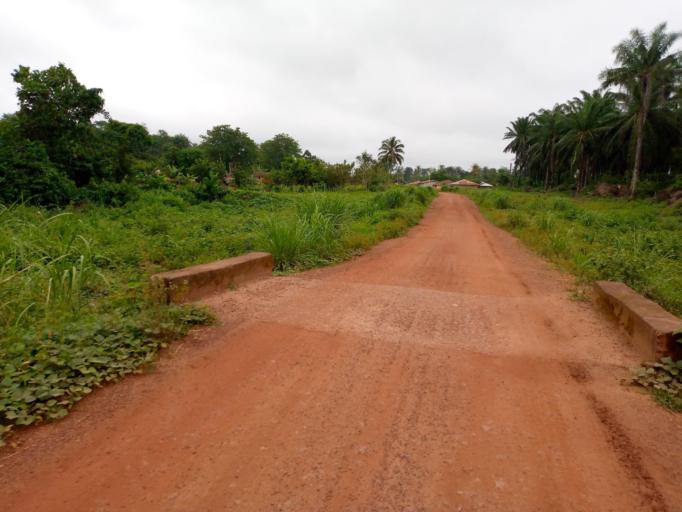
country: SL
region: Southern Province
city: Sumbuya
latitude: 7.5983
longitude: -12.0840
